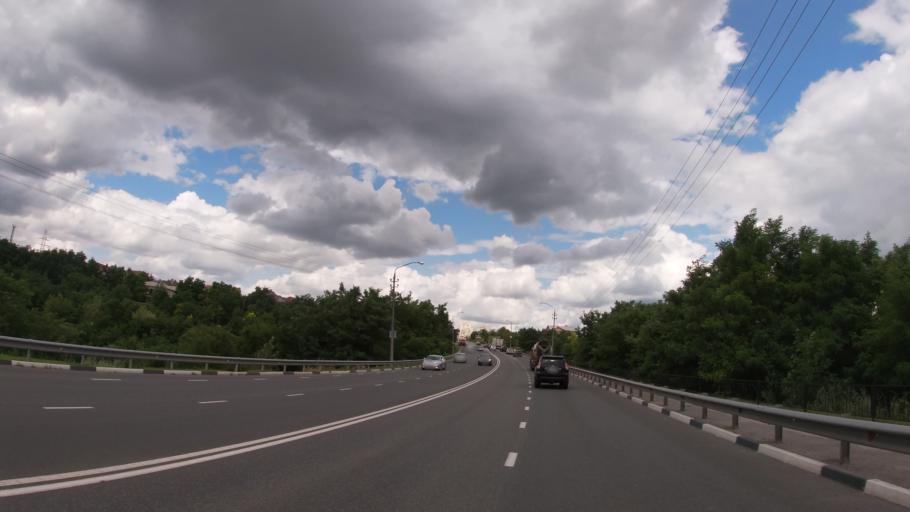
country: RU
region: Belgorod
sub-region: Belgorodskiy Rayon
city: Belgorod
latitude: 50.5589
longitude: 36.5864
